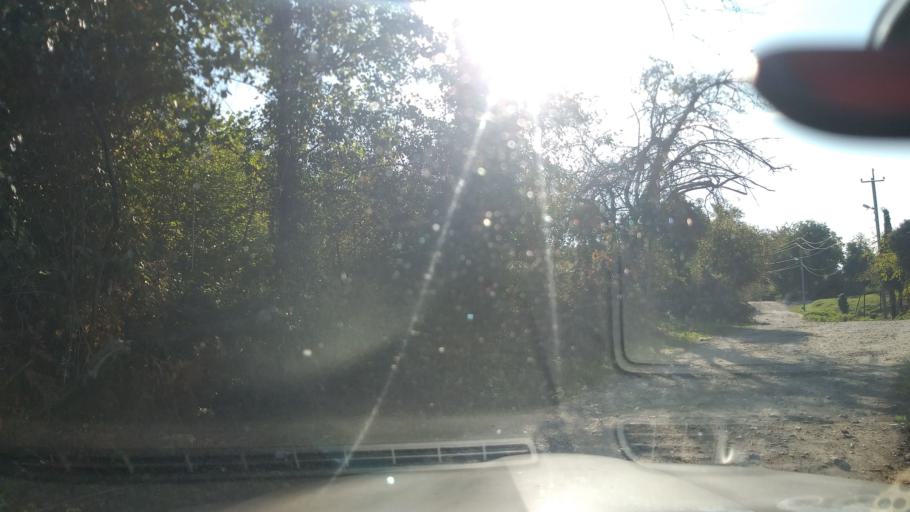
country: GE
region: Abkhazia
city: Stantsiya Novyy Afon
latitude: 43.0624
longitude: 40.8907
